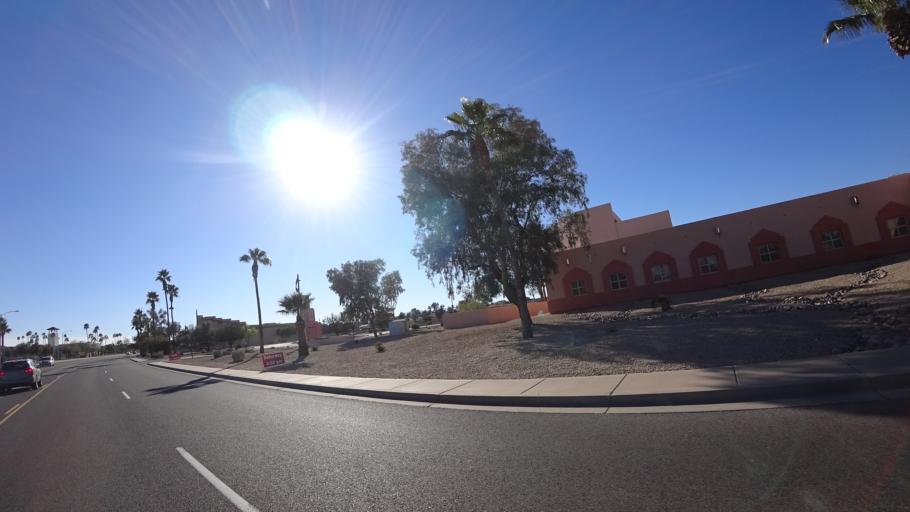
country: US
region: Arizona
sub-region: Maricopa County
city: Sun City West
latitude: 33.6653
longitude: -112.3571
